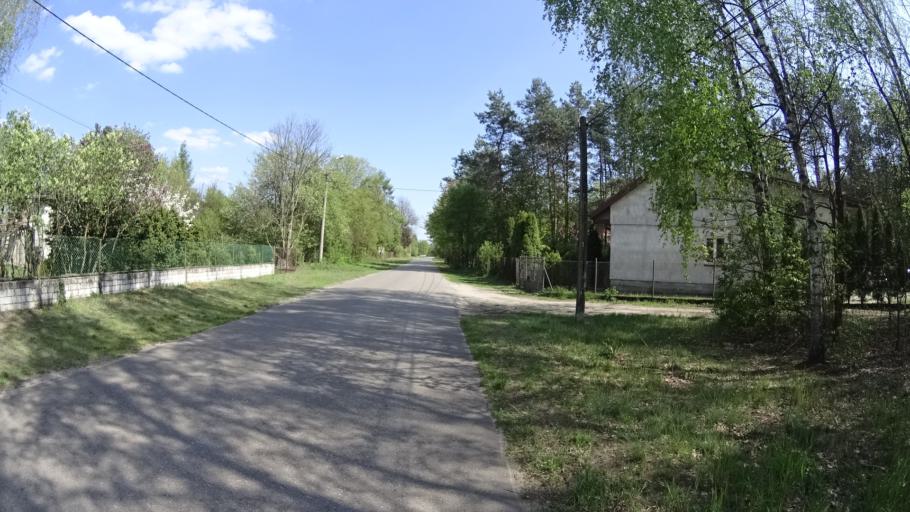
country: PL
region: Masovian Voivodeship
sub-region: Powiat warszawski zachodni
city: Izabelin
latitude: 52.3147
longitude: 20.8043
